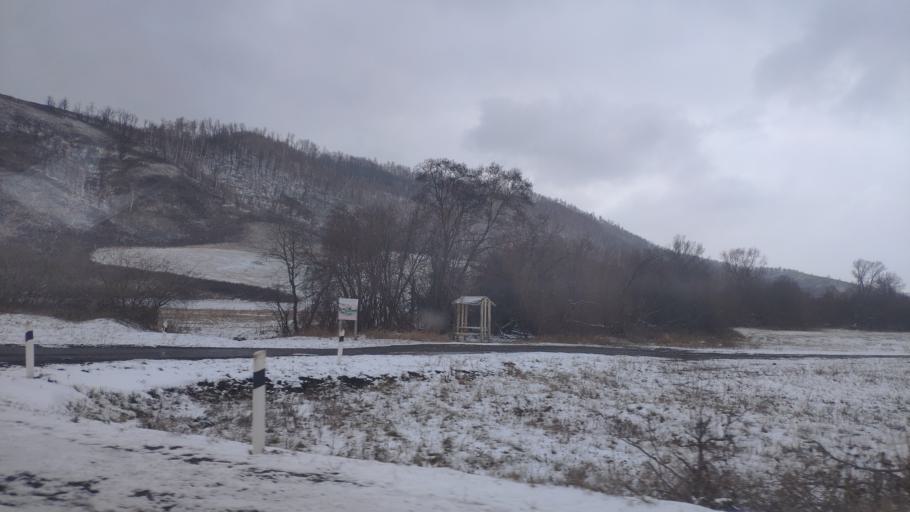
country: RU
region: Bashkortostan
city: Isyangulovo
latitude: 52.1606
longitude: 56.9234
